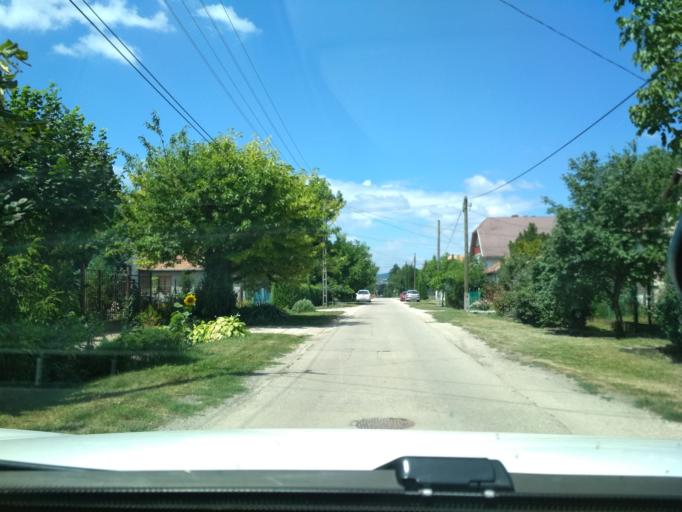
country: HU
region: Fejer
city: Kapolnasnyek
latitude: 47.2186
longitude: 18.6682
